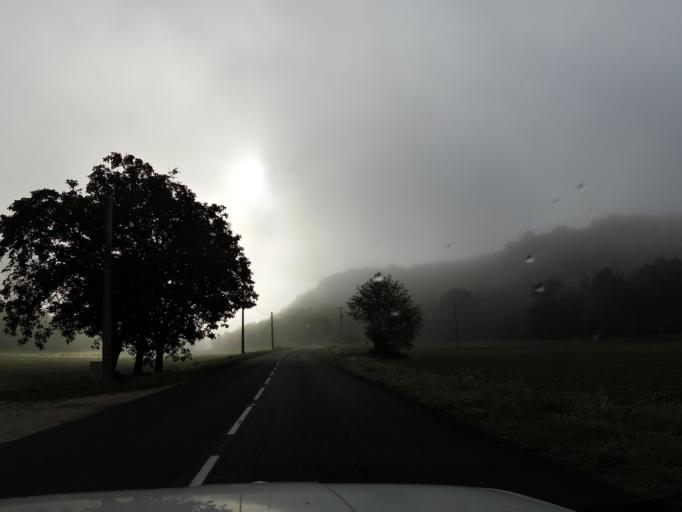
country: FR
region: Rhone-Alpes
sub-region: Departement de l'Isere
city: Creys-Mepieu
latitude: 45.7609
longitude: 5.4896
